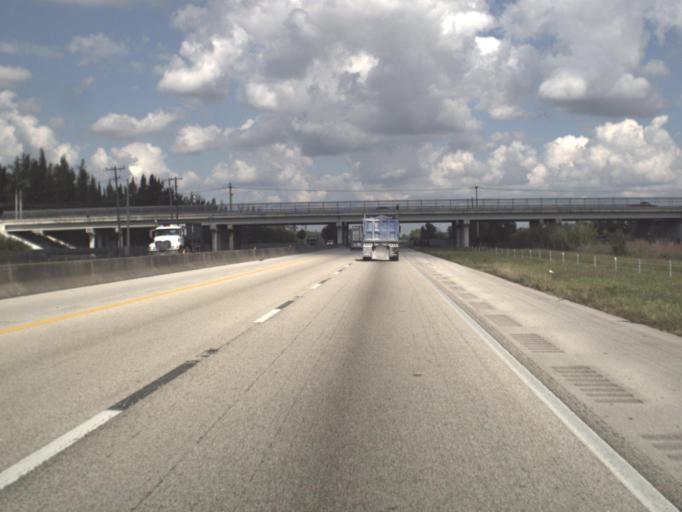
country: US
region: Florida
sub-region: Palm Beach County
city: Greenacres City
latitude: 26.6491
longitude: -80.1740
